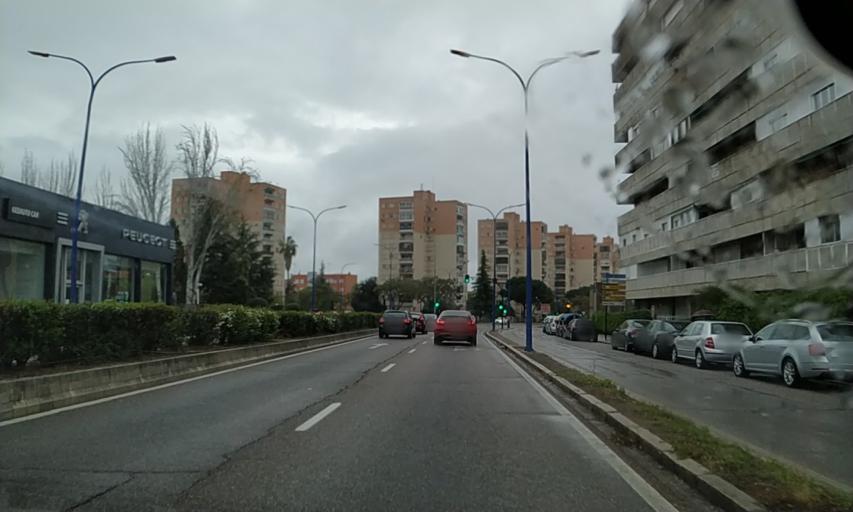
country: ES
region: Extremadura
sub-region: Provincia de Badajoz
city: Badajoz
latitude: 38.8722
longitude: -6.9801
